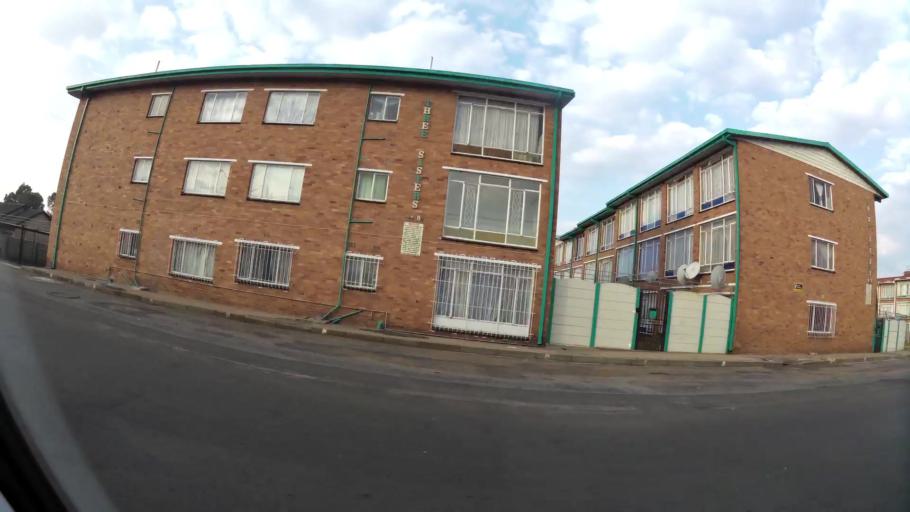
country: ZA
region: Gauteng
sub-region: Ekurhuleni Metropolitan Municipality
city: Germiston
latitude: -26.2508
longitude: 28.1944
